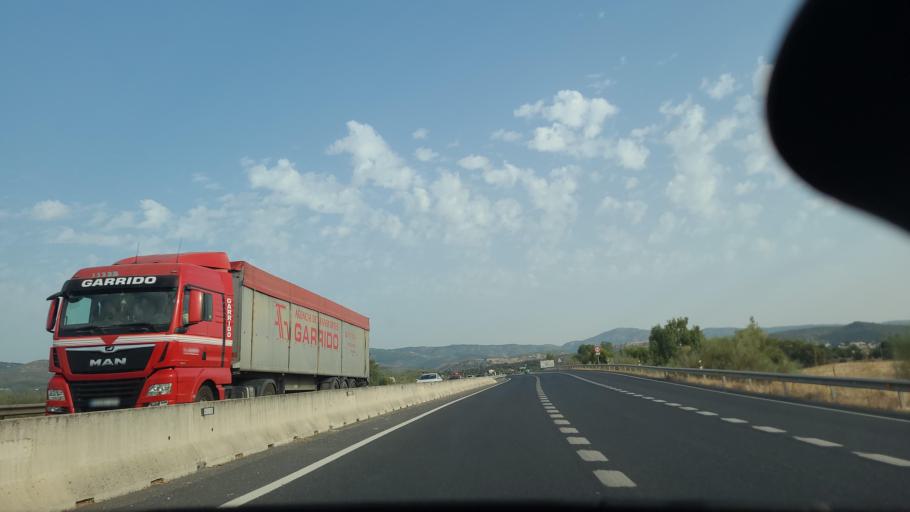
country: ES
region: Andalusia
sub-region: Province of Cordoba
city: Cordoba
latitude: 37.9165
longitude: -4.7599
